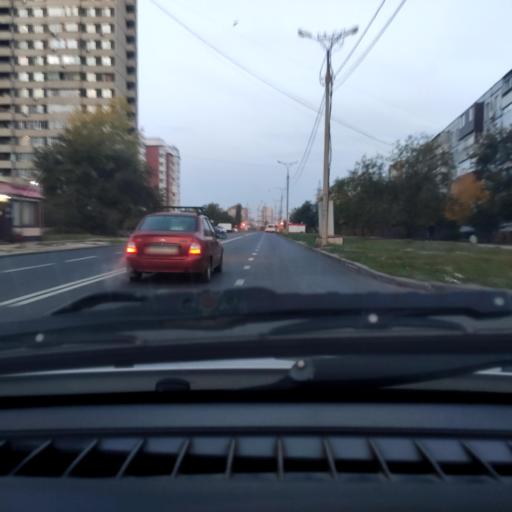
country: RU
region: Samara
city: Zhigulevsk
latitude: 53.4709
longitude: 49.5351
